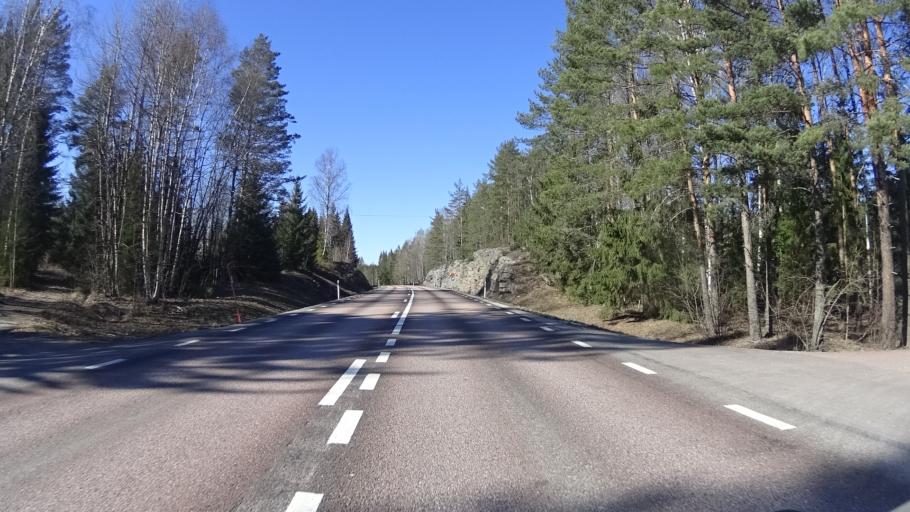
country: SE
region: Vaermland
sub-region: Karlstads Kommun
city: Edsvalla
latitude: 59.6105
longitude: 12.9883
